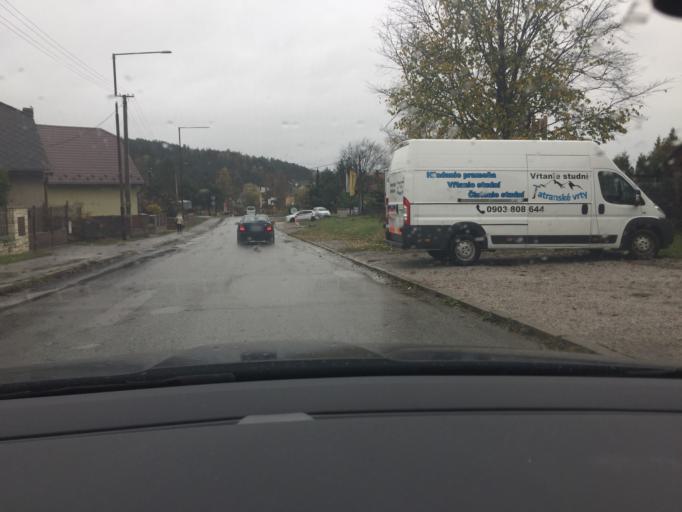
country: SK
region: Presovsky
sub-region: Okres Presov
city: Kezmarok
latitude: 49.1505
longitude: 20.4286
